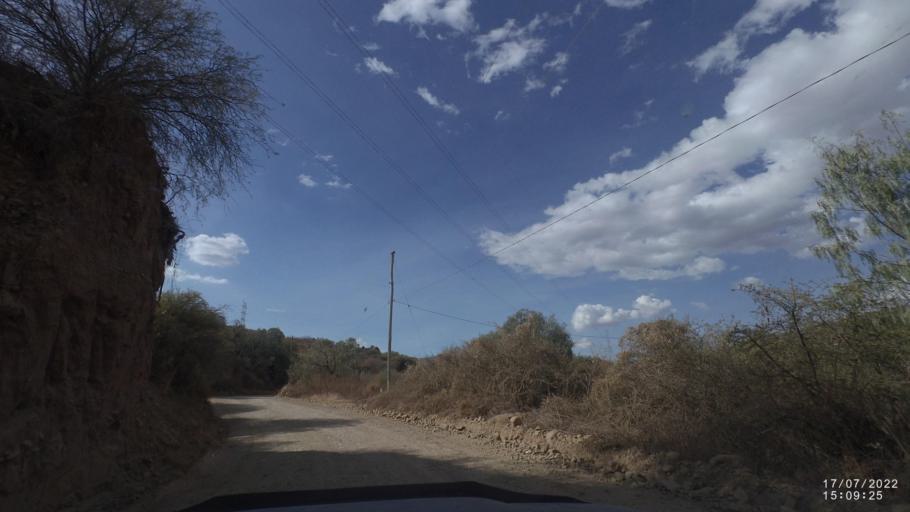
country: BO
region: Cochabamba
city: Capinota
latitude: -17.5742
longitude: -66.2661
